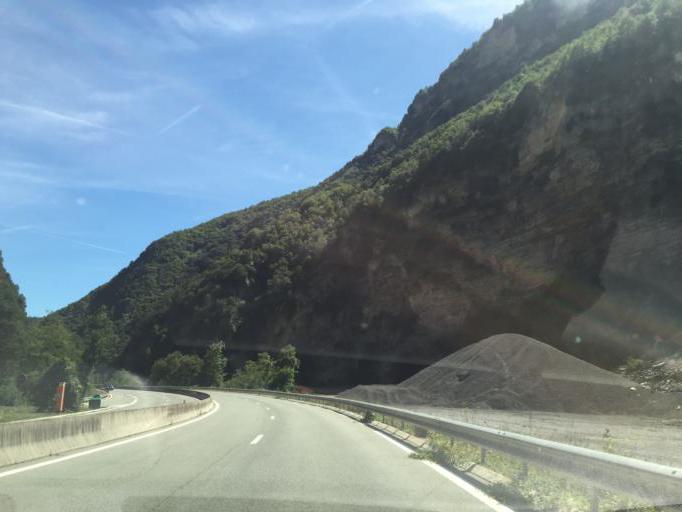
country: FR
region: Provence-Alpes-Cote d'Azur
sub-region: Departement des Alpes-Maritimes
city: Saint-Martin-Vesubie
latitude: 44.0161
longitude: 7.1309
